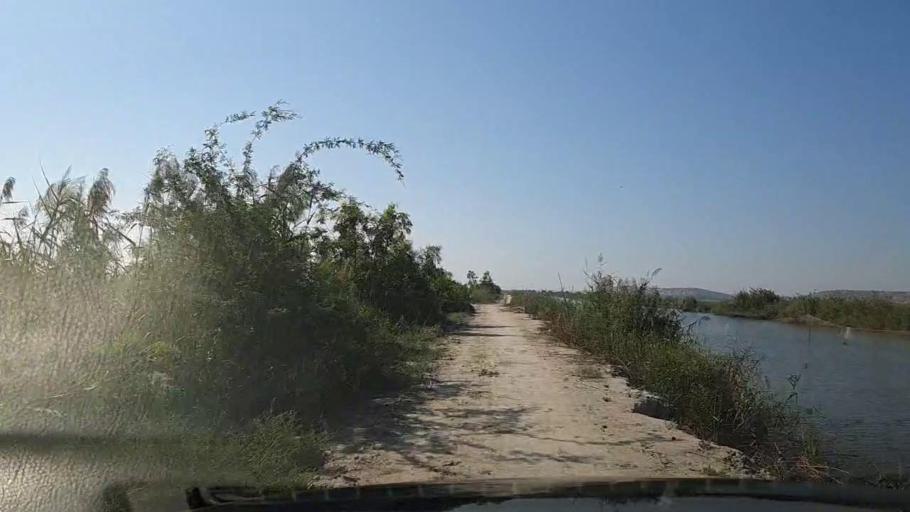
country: PK
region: Sindh
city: Thatta
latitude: 24.6909
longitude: 67.8941
